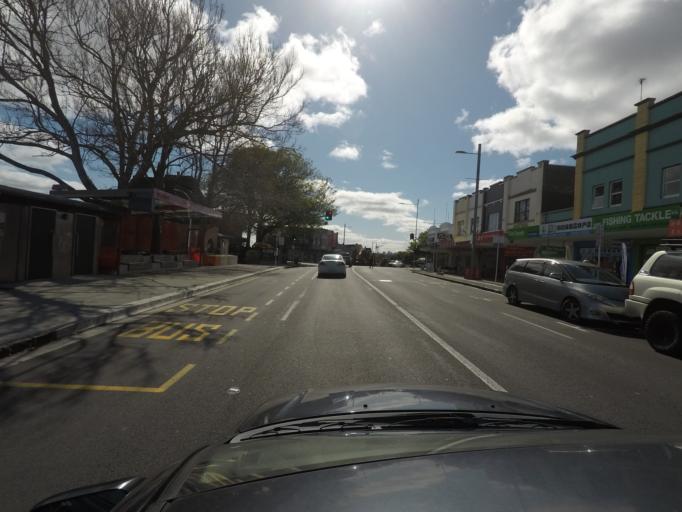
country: NZ
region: Auckland
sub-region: Auckland
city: Rosebank
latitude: -36.8845
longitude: 174.7150
